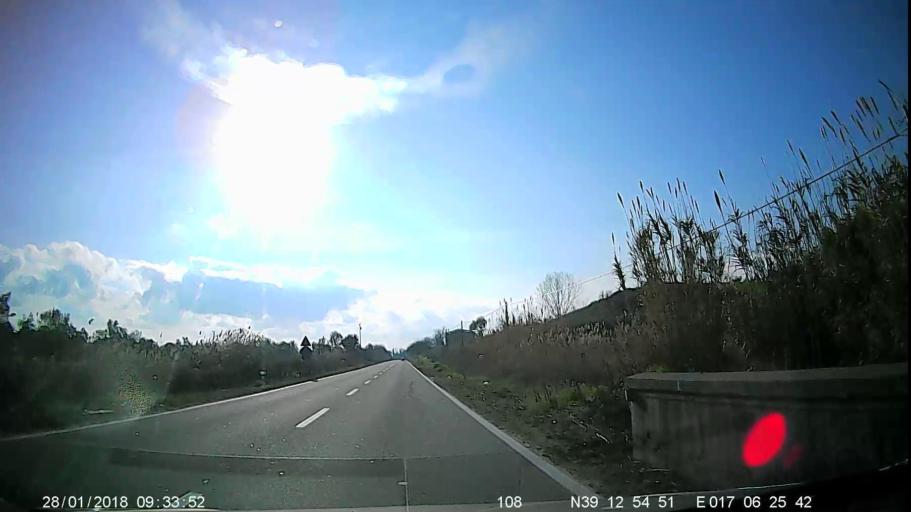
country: IT
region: Calabria
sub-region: Provincia di Crotone
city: Tronca
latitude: 39.2148
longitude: 17.1073
